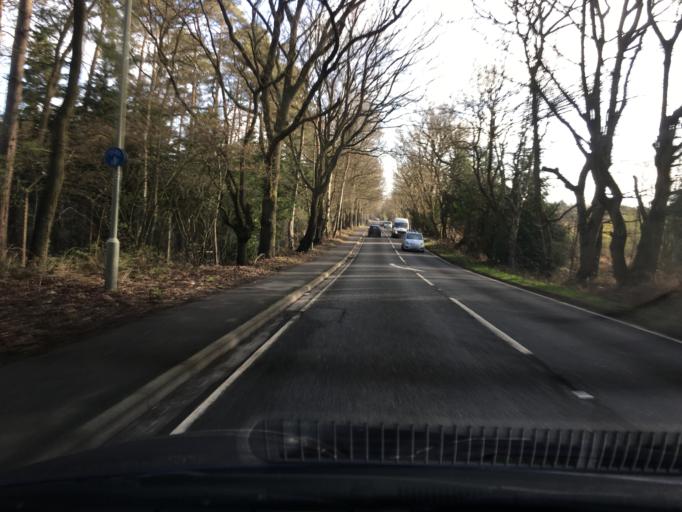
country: GB
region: England
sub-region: Bracknell Forest
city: Crowthorne
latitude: 51.3794
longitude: -0.7792
